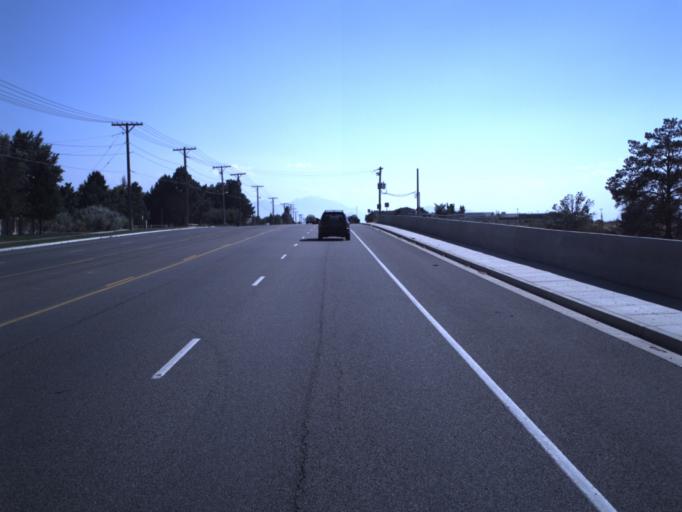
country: US
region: Utah
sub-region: Utah County
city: Cedar Hills
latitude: 40.4241
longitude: -111.7736
